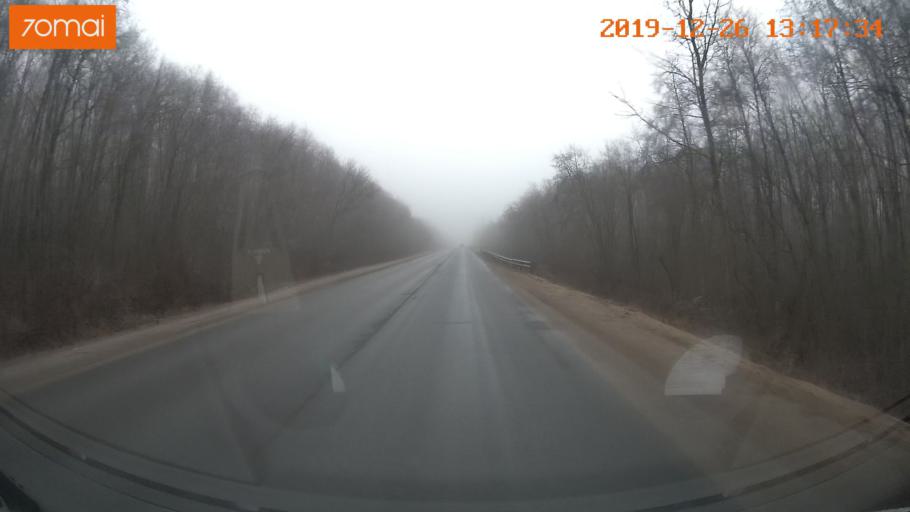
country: RU
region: Vologda
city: Cherepovets
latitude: 58.9681
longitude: 38.1158
